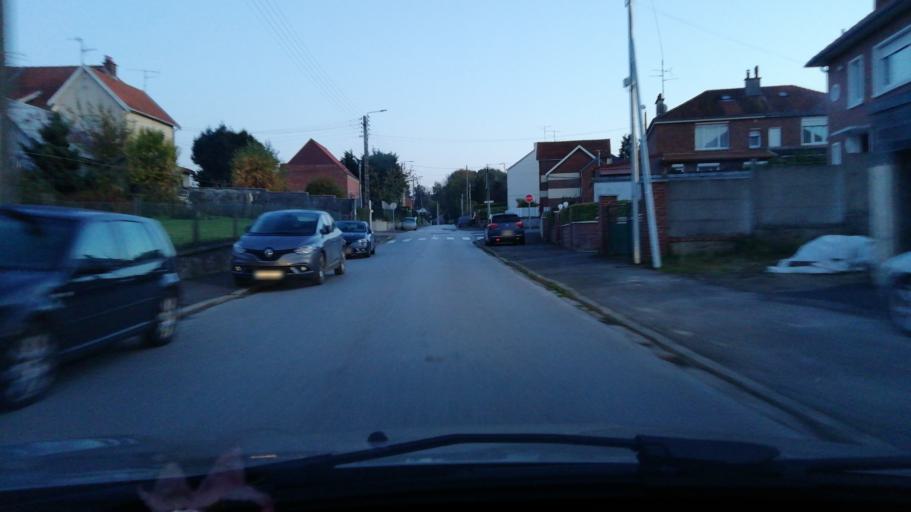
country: FR
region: Nord-Pas-de-Calais
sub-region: Departement du Nord
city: Marpent
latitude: 50.2895
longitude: 4.0836
